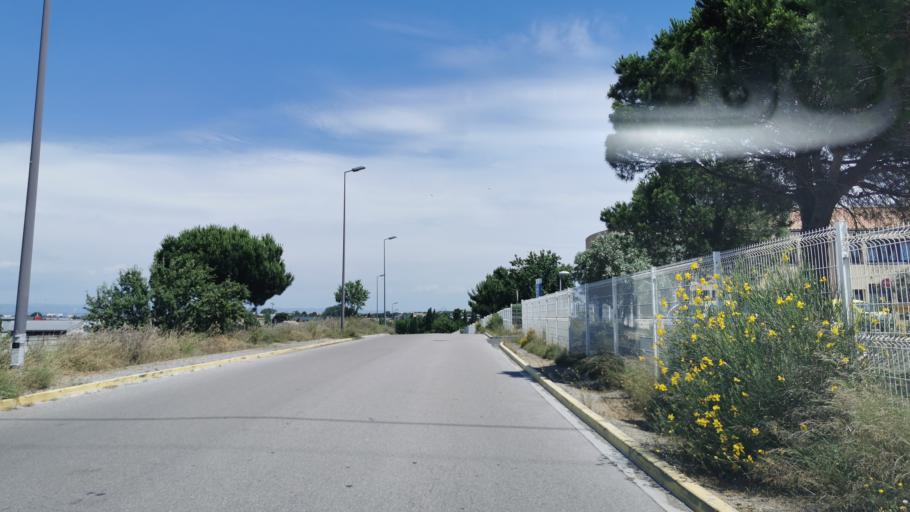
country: FR
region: Languedoc-Roussillon
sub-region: Departement de l'Aude
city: Narbonne
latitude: 43.1658
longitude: 2.9901
